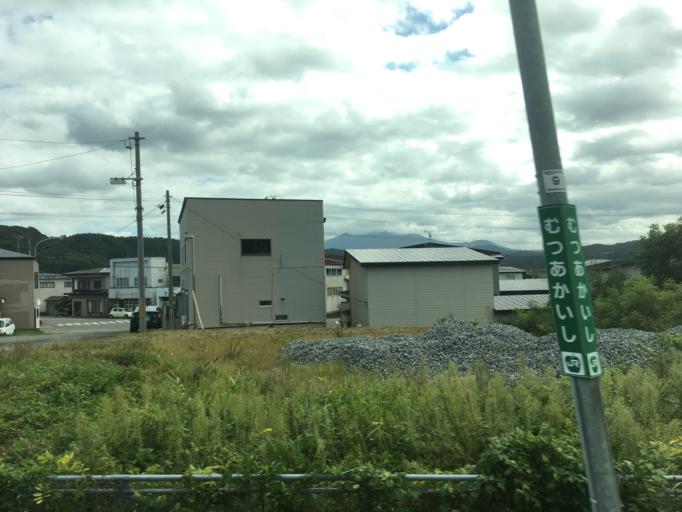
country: JP
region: Aomori
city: Shimokizukuri
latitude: 40.7616
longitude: 140.1622
